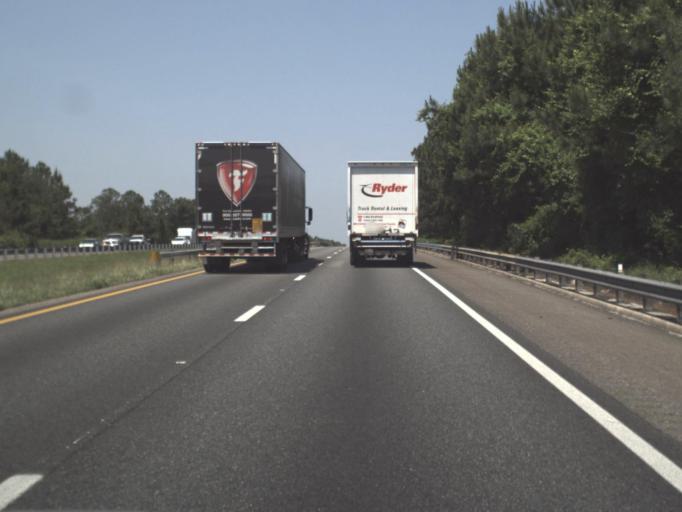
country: US
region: Florida
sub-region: Duval County
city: Baldwin
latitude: 30.3048
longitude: -81.8969
